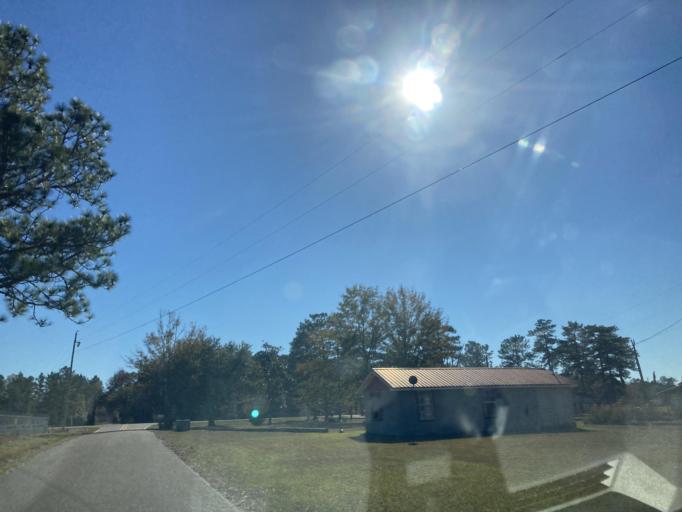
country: US
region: Mississippi
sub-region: Lamar County
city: Sumrall
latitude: 31.2871
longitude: -89.6454
